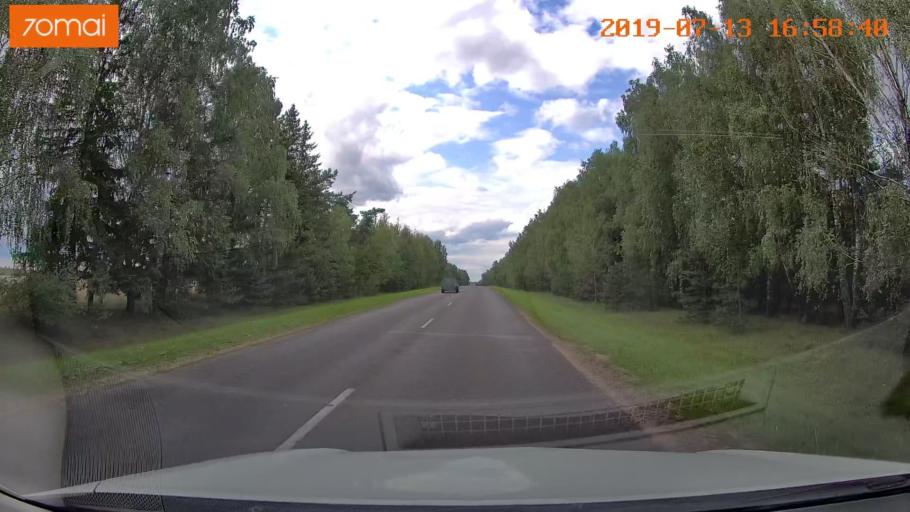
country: BY
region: Mogilev
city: Kirawsk
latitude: 53.2912
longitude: 29.4399
